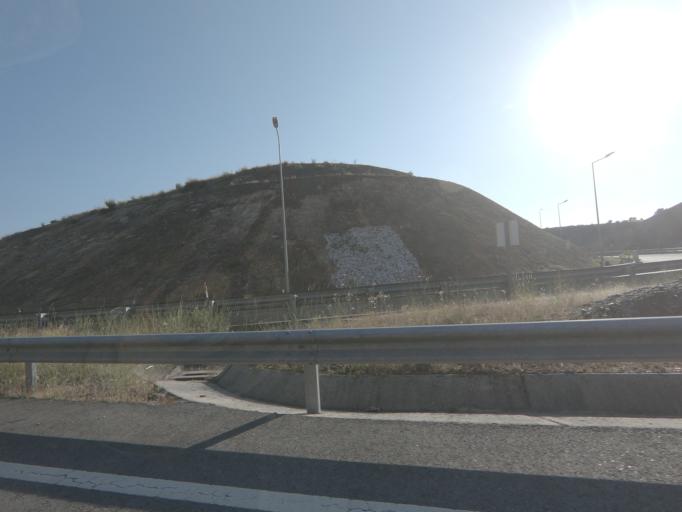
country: PT
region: Vila Real
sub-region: Chaves
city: Chaves
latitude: 41.8054
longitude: -7.4123
